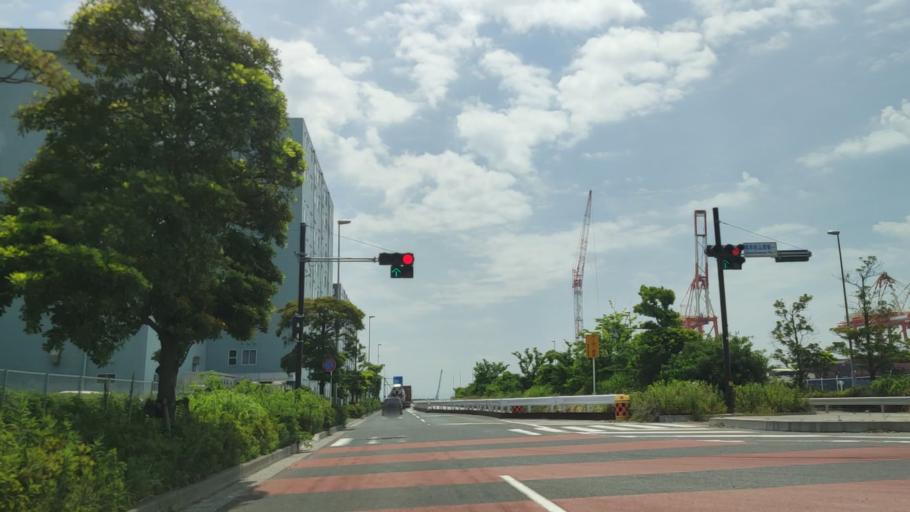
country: JP
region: Kanagawa
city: Yokohama
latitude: 35.4067
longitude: 139.6827
